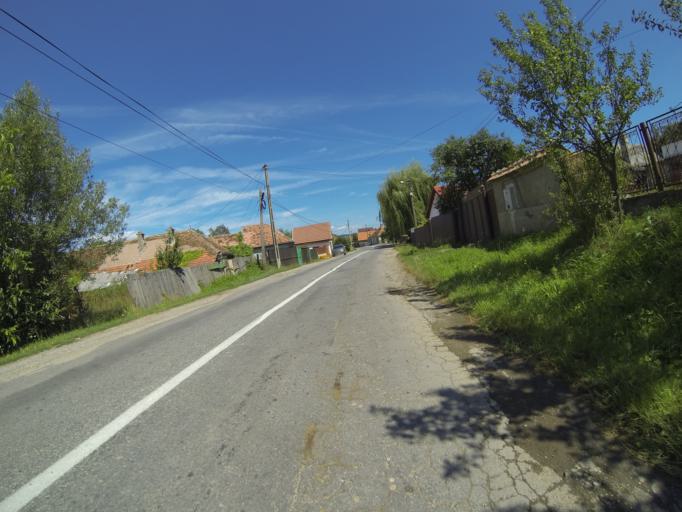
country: RO
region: Brasov
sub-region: Comuna Sinca Veche
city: Sinca Veche
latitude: 45.7626
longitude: 25.1582
